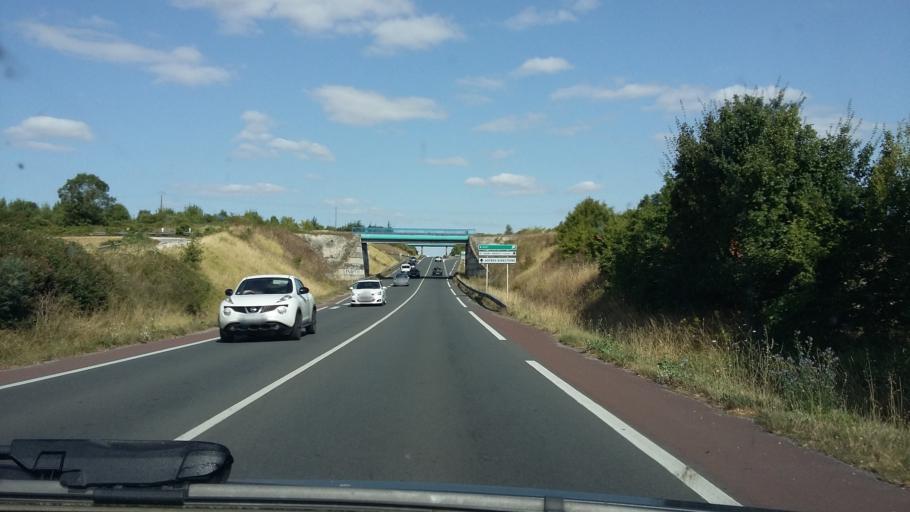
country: FR
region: Poitou-Charentes
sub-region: Departement de la Charente-Maritime
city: Saint-Jean-d'Angely
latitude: 45.9560
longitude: -0.5221
